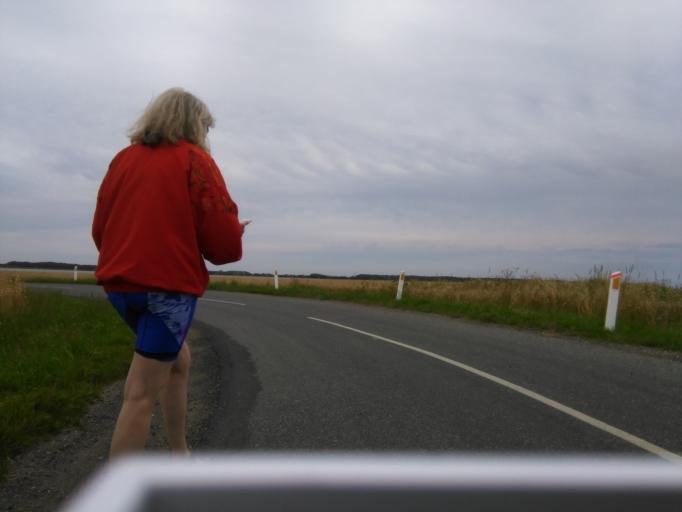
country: DK
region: Central Jutland
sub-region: Odder Kommune
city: Odder
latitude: 55.8625
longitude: 10.1143
